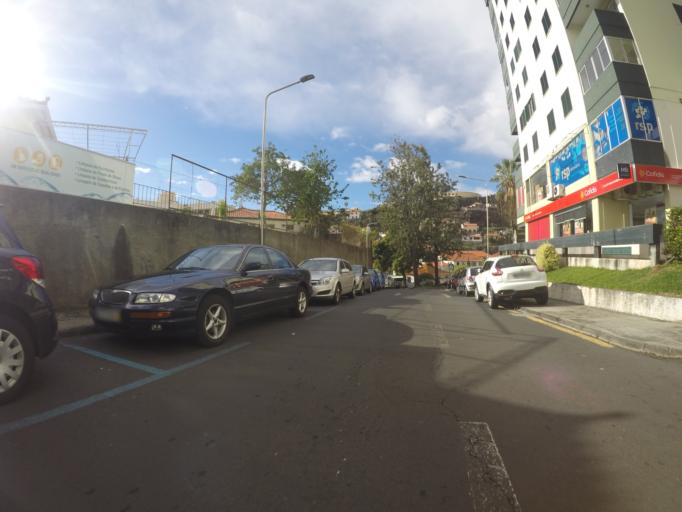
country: PT
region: Madeira
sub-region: Funchal
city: Nossa Senhora do Monte
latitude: 32.6564
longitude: -16.9141
